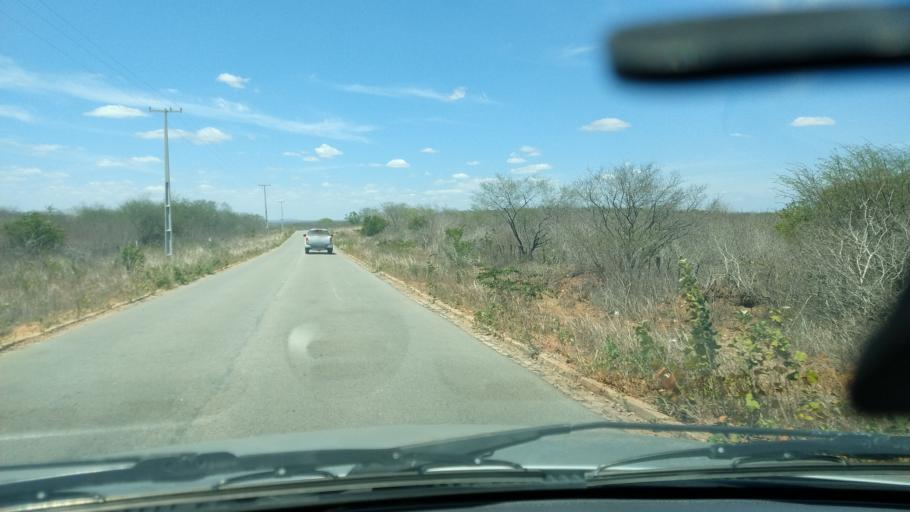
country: BR
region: Rio Grande do Norte
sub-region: Sao Paulo Do Potengi
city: Sao Paulo do Potengi
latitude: -5.9130
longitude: -35.5922
